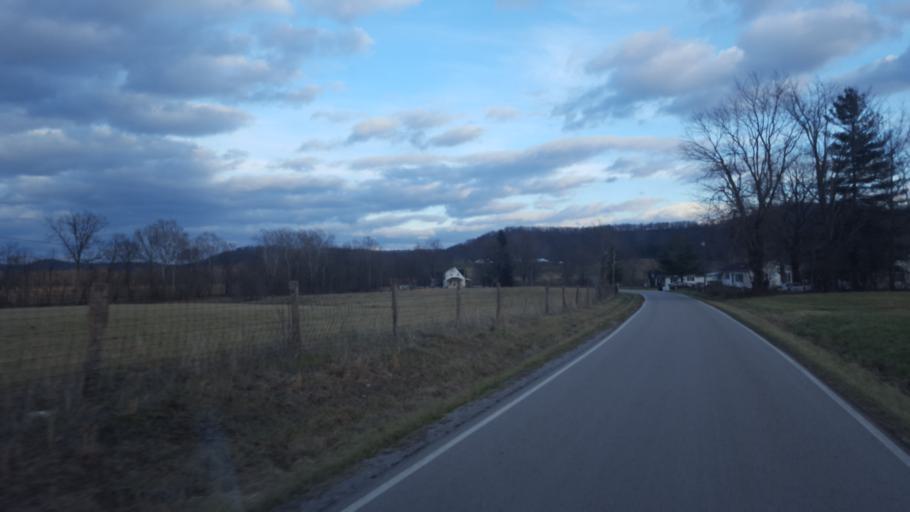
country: US
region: Kentucky
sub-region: Fleming County
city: Flemingsburg
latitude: 38.4959
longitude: -83.5680
